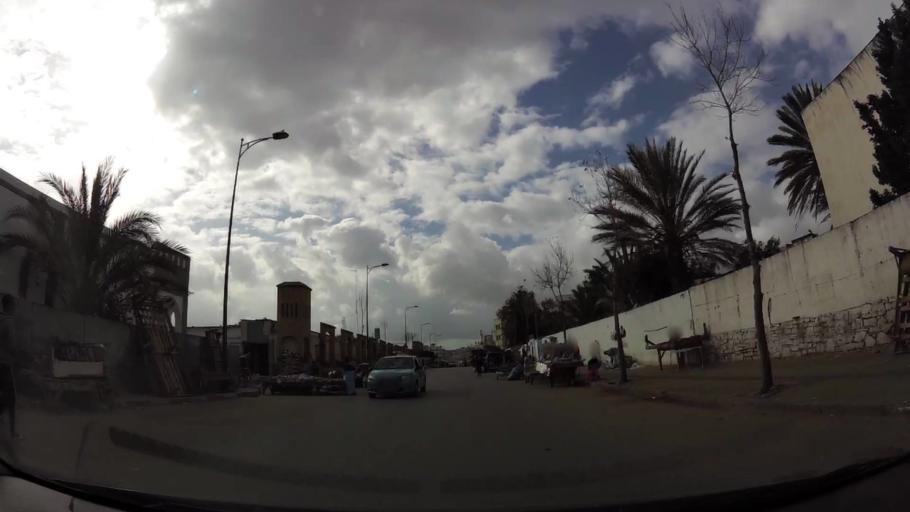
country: MA
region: Tanger-Tetouan
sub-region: Tanger-Assilah
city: Tangier
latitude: 35.7656
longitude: -5.8240
